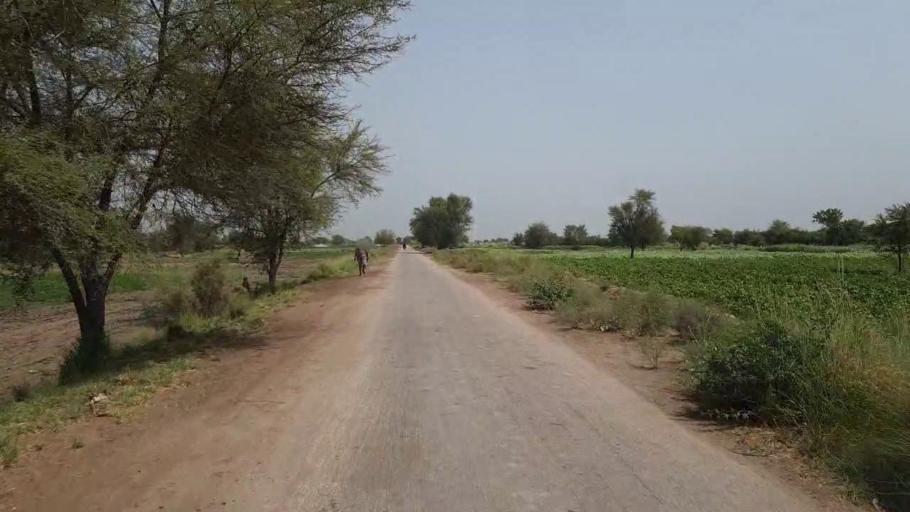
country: PK
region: Sindh
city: Nawabshah
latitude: 26.2628
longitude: 68.3182
